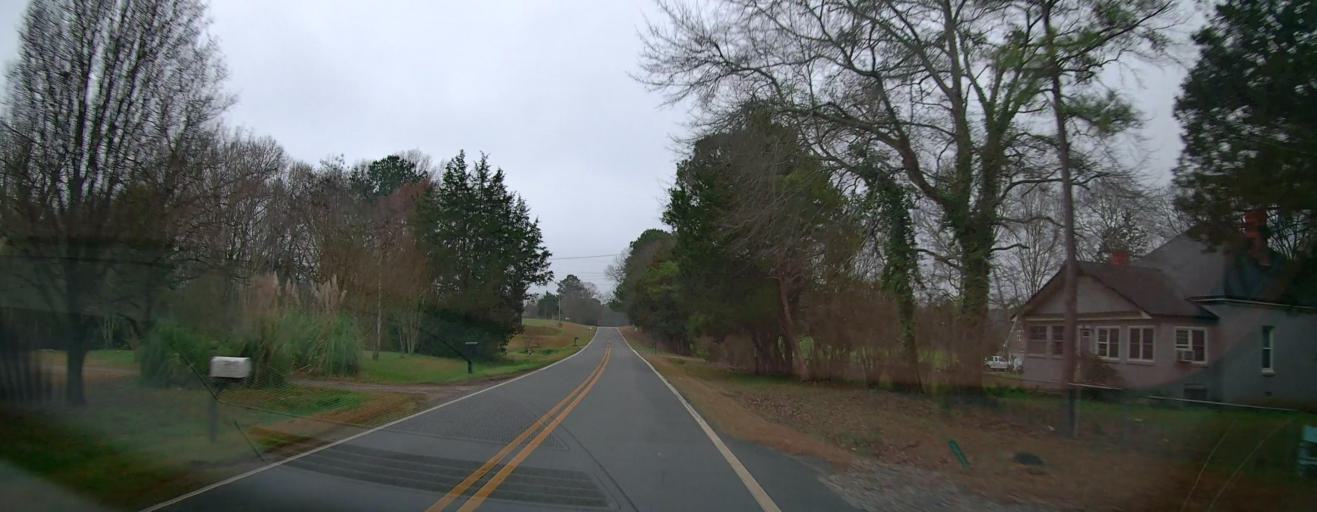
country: US
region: Georgia
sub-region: Monroe County
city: Forsyth
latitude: 33.1168
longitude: -83.9737
